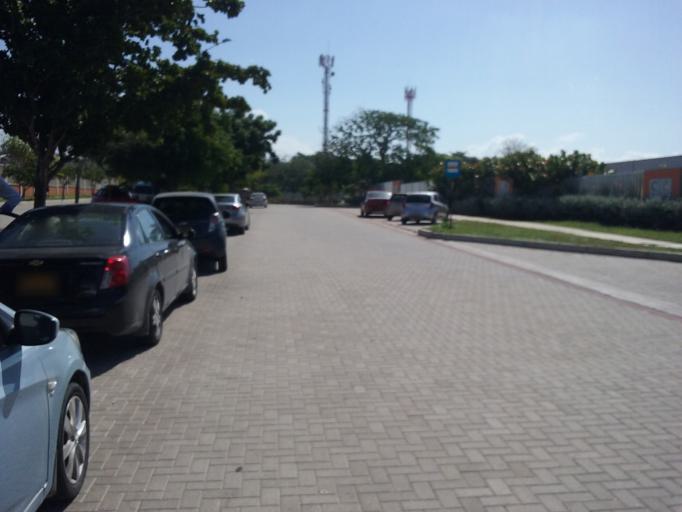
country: CO
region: Atlantico
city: Barranquilla
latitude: 11.0223
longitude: -74.8521
